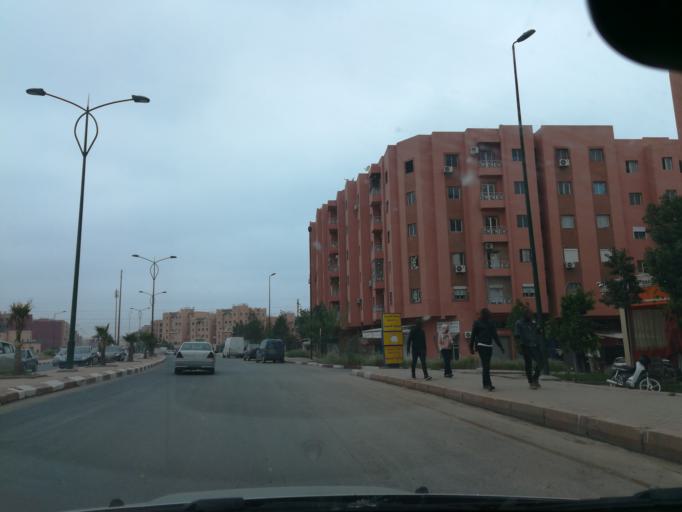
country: MA
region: Marrakech-Tensift-Al Haouz
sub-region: Marrakech
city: Marrakesh
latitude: 31.6720
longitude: -8.0147
